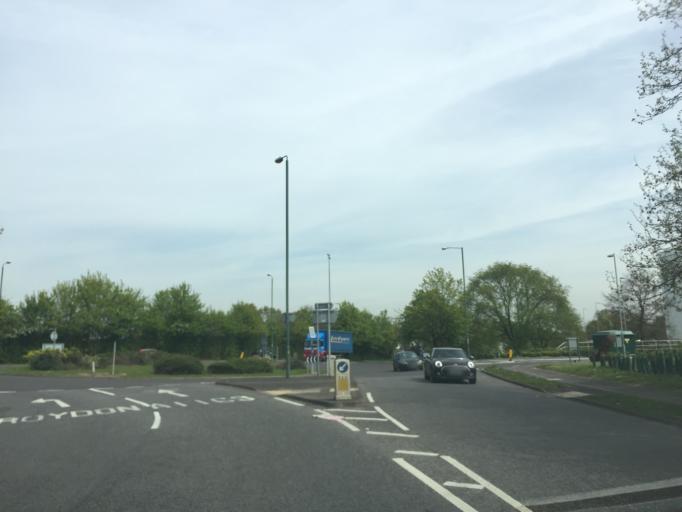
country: GB
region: England
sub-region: Essex
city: Roydon
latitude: 51.7695
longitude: 0.0680
